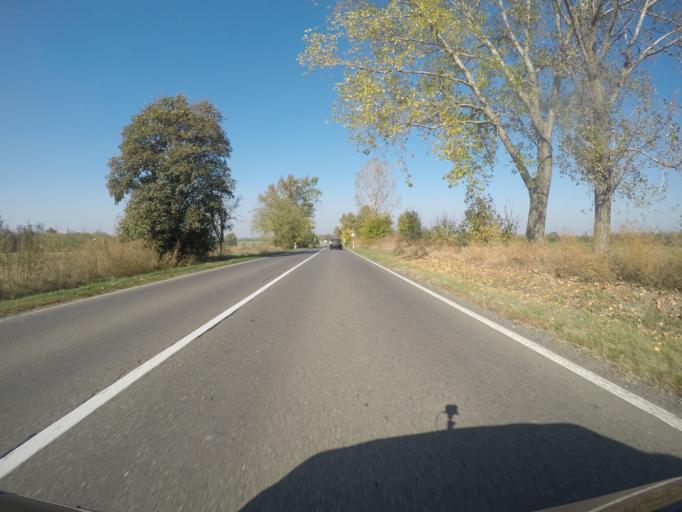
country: HU
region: Tolna
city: Tengelic
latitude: 46.5314
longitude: 18.6565
